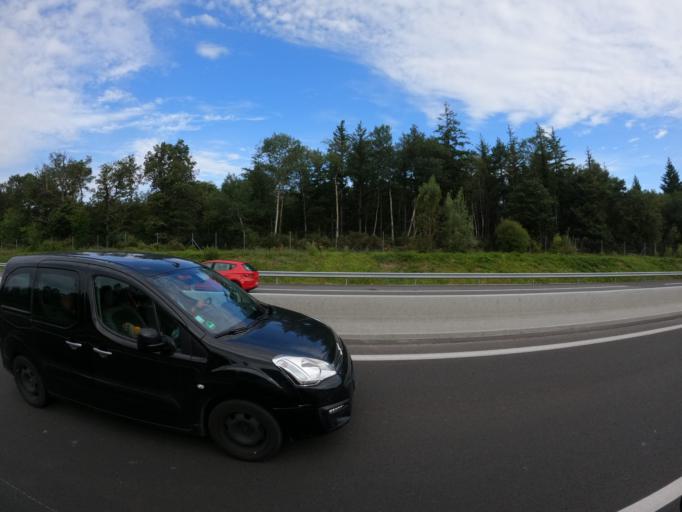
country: FR
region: Centre
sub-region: Departement d'Indre-et-Loire
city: Langeais
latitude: 47.3309
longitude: 0.3458
